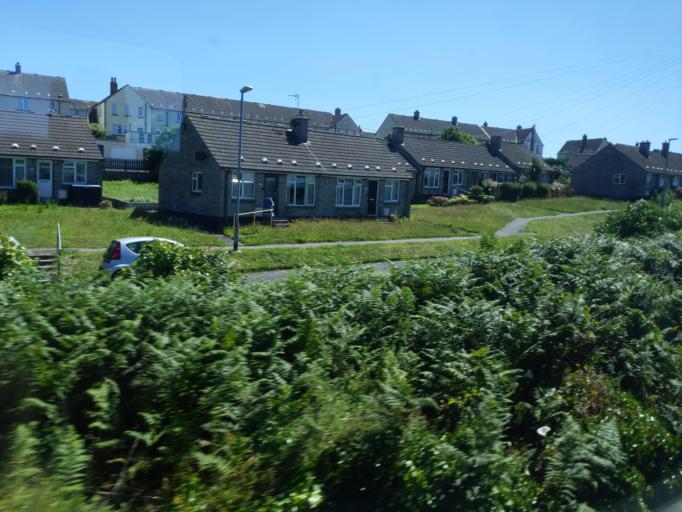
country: GB
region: England
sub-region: Cornwall
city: Hayle
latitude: 50.1874
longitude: -5.4165
